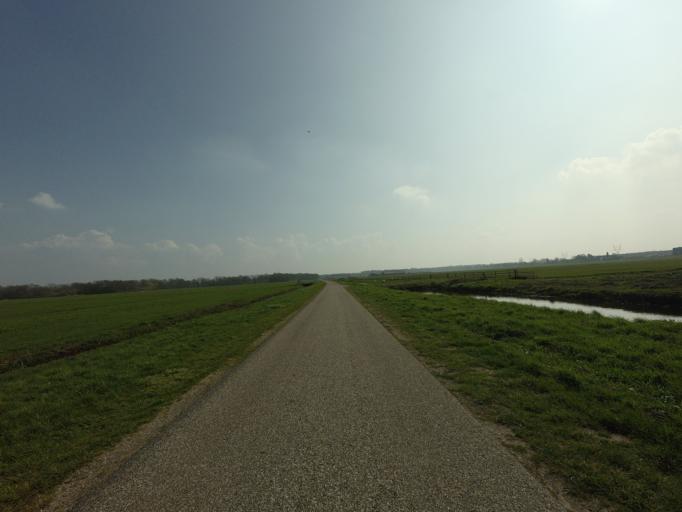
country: NL
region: North Holland
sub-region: Gemeente Bussum
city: Bussum
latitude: 52.2742
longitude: 5.1247
